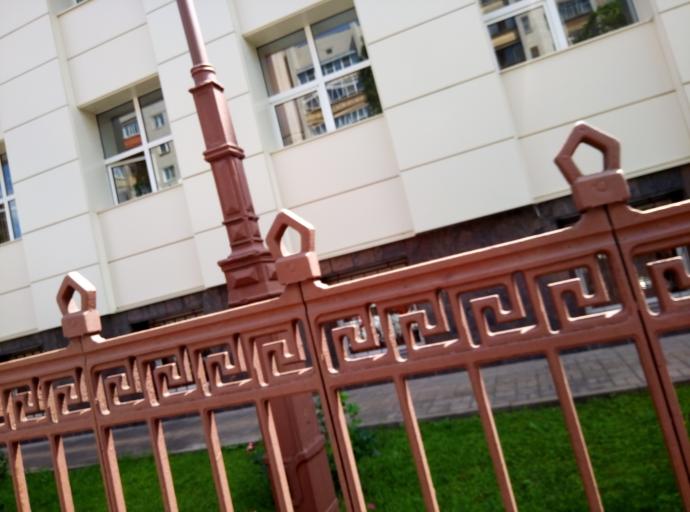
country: RU
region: Kursk
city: Kursk
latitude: 51.7384
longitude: 36.1873
